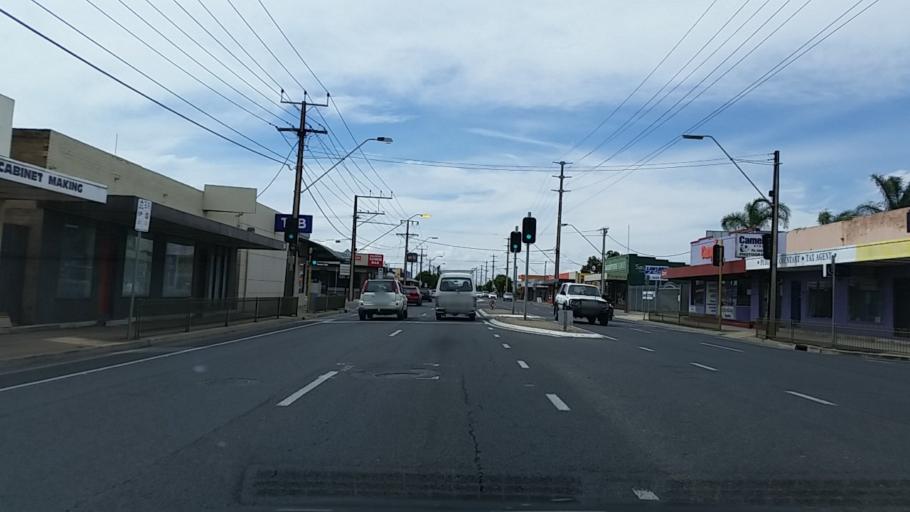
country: AU
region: South Australia
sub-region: City of West Torrens
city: Plympton
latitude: -34.9394
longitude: 138.5530
